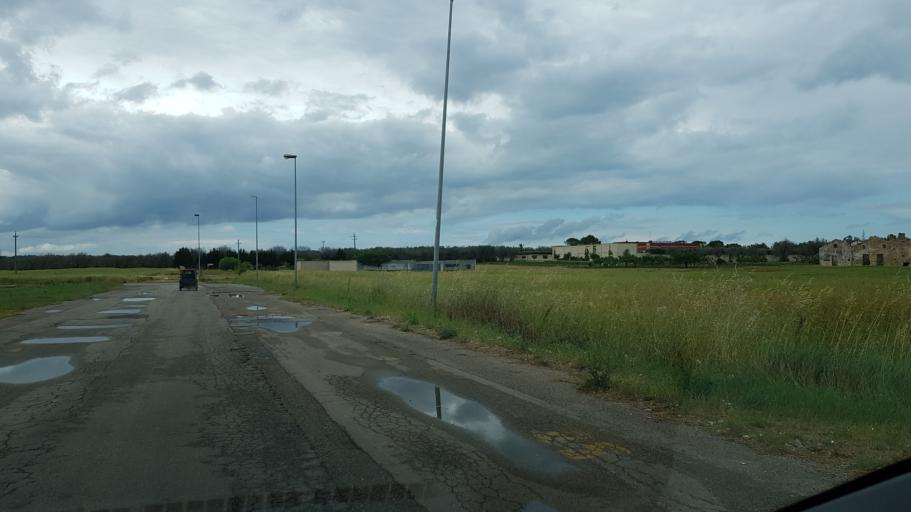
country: IT
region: Apulia
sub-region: Provincia di Brindisi
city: Torchiarolo
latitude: 40.4885
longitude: 18.0443
